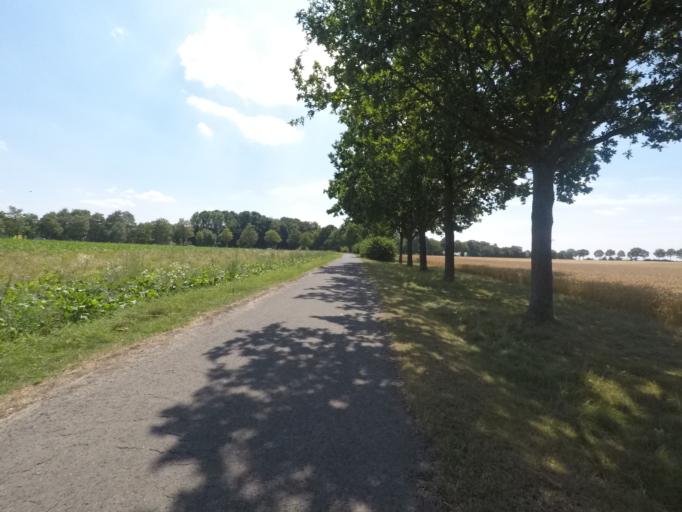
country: DE
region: North Rhine-Westphalia
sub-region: Regierungsbezirk Detmold
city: Bielefeld
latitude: 52.0527
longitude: 8.5879
